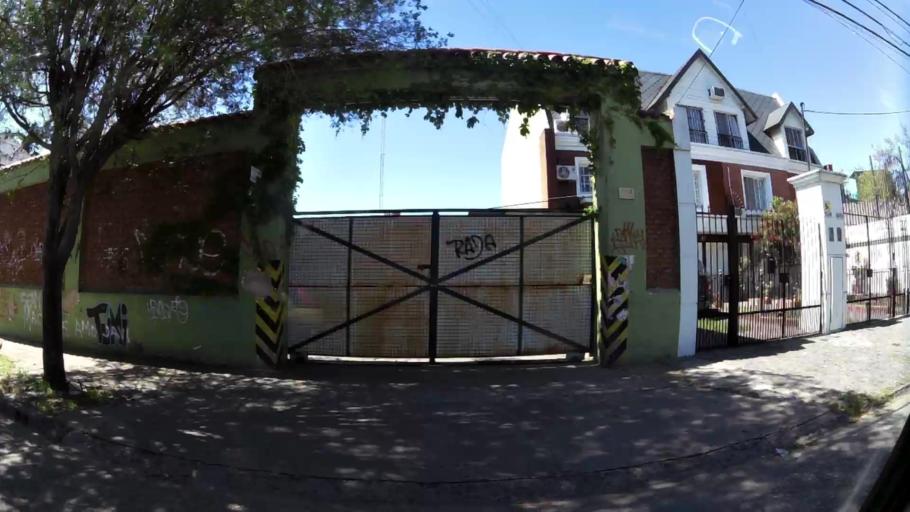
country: AR
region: Buenos Aires
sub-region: Partido de Vicente Lopez
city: Olivos
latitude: -34.5199
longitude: -58.4961
